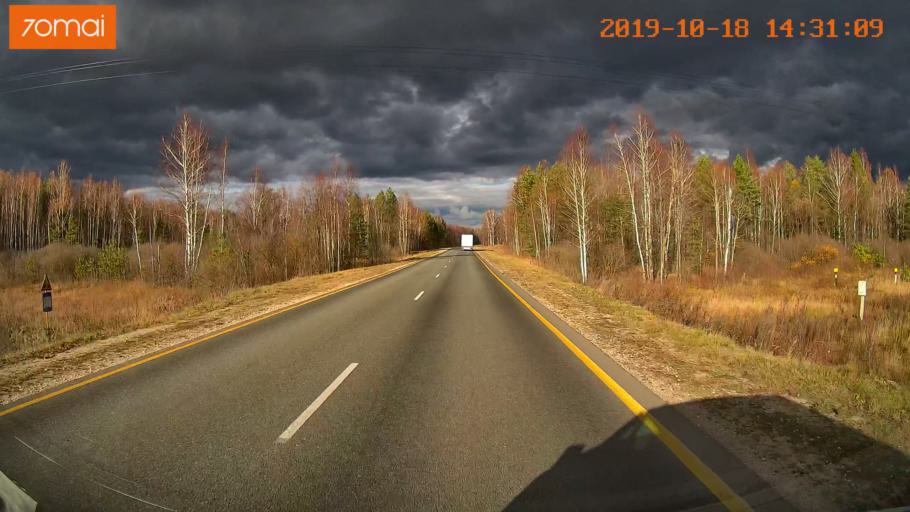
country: RU
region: Rjazan
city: Tuma
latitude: 55.1789
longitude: 40.5686
